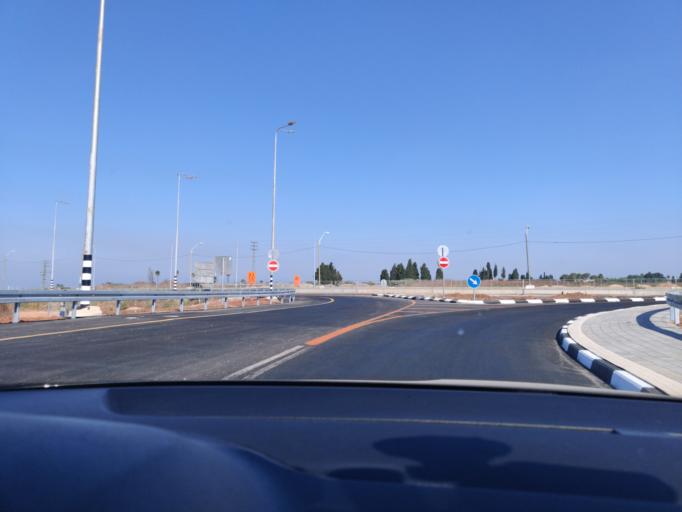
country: IL
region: Central District
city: Elyakhin
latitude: 32.4571
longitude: 34.9842
